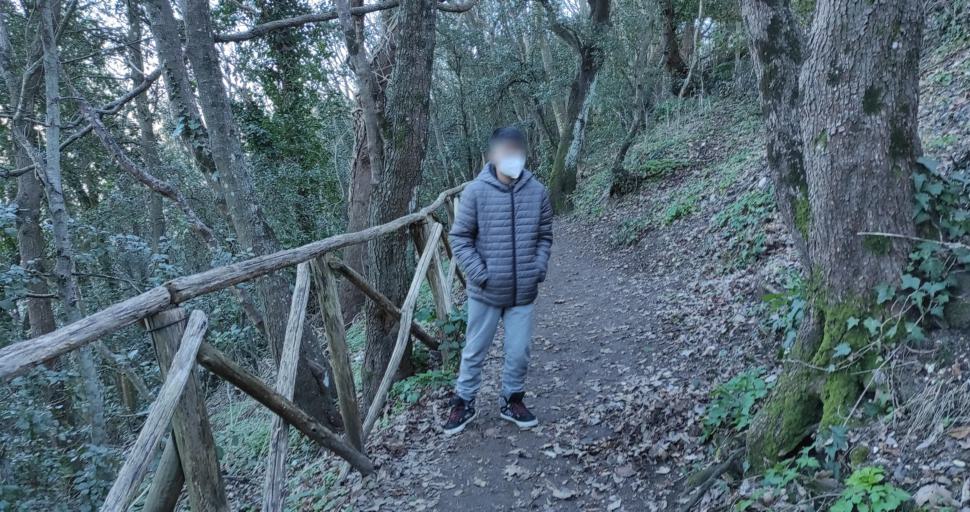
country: IT
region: The Marches
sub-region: Provincia di Ancona
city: Sirolo
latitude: 43.5474
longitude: 13.6169
